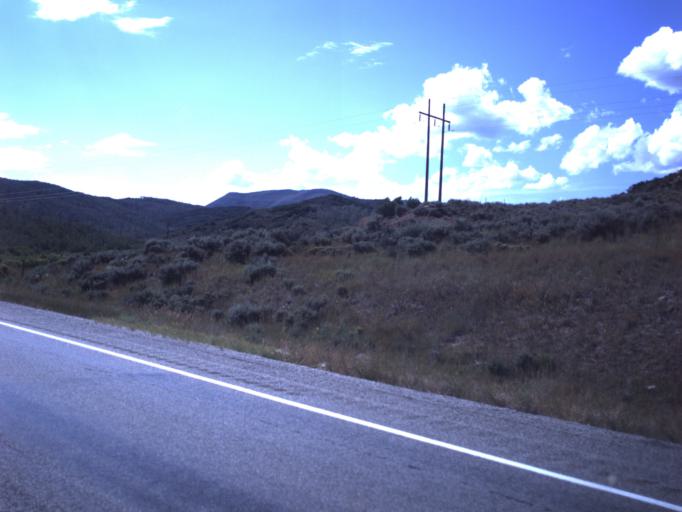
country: US
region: Utah
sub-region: Summit County
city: Francis
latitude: 40.1995
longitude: -110.9974
